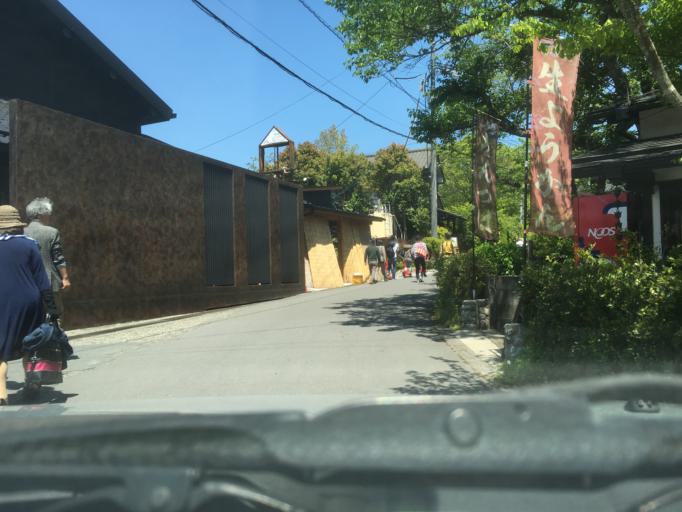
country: JP
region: Oita
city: Beppu
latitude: 33.2679
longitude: 131.3676
